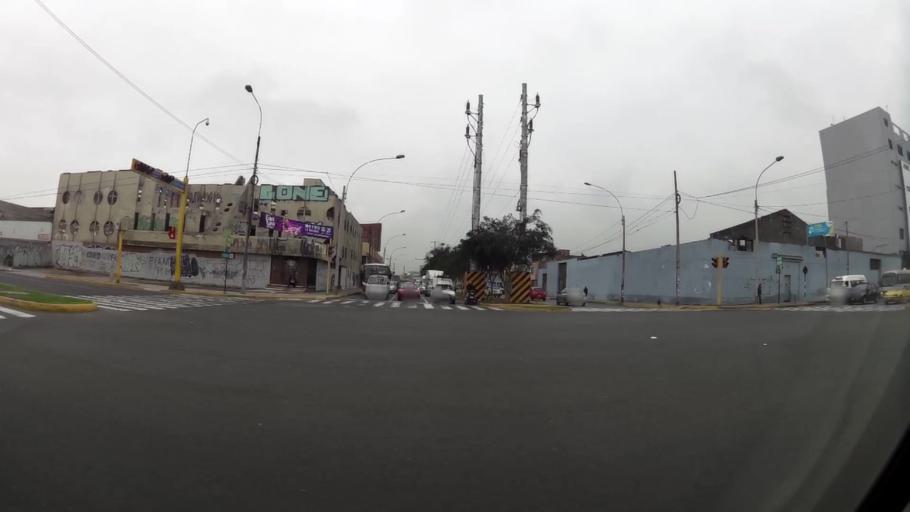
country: PE
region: Lima
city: Lima
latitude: -12.0566
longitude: -77.0616
